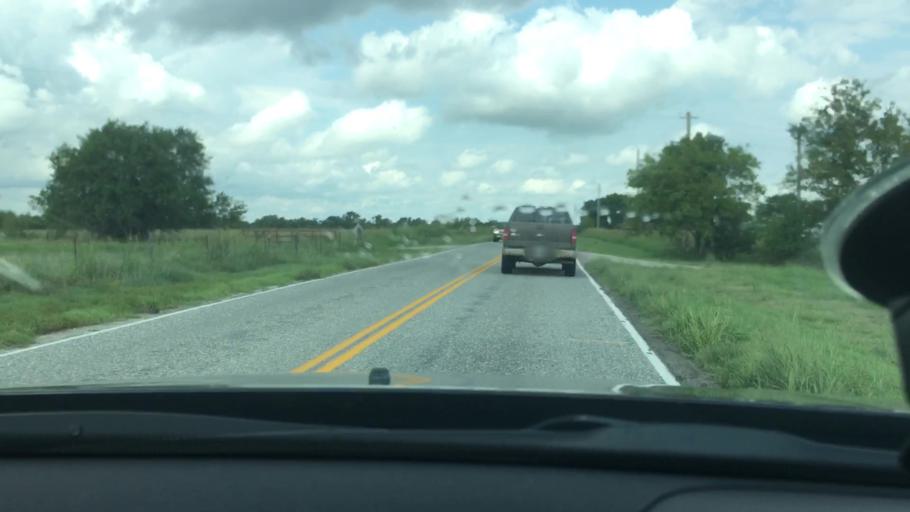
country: US
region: Oklahoma
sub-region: Johnston County
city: Tishomingo
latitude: 34.1829
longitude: -96.5133
